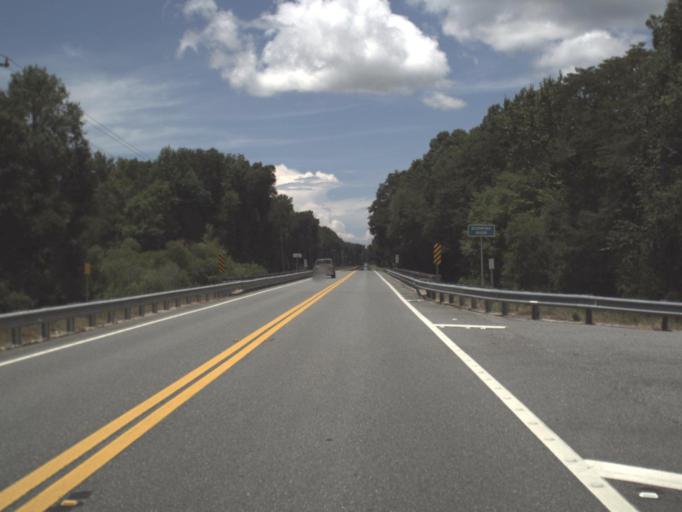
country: US
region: Florida
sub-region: Taylor County
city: Perry
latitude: 30.1423
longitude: -83.8656
